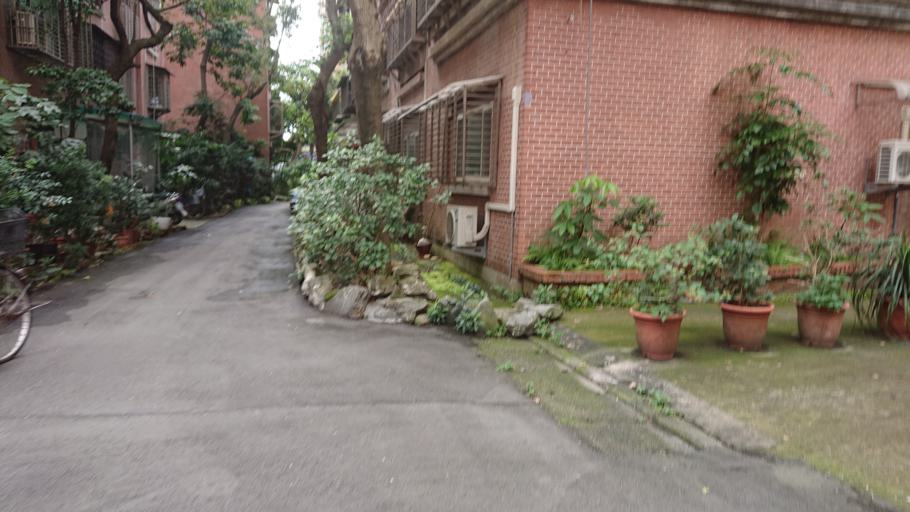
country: TW
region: Taipei
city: Taipei
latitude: 25.0296
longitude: 121.5400
